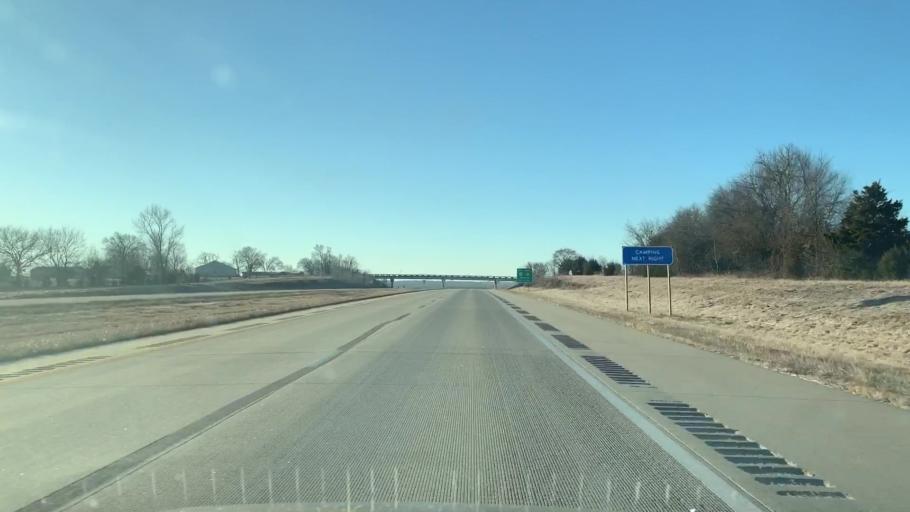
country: US
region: Kansas
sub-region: Bourbon County
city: Fort Scott
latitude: 37.8666
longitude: -94.7042
